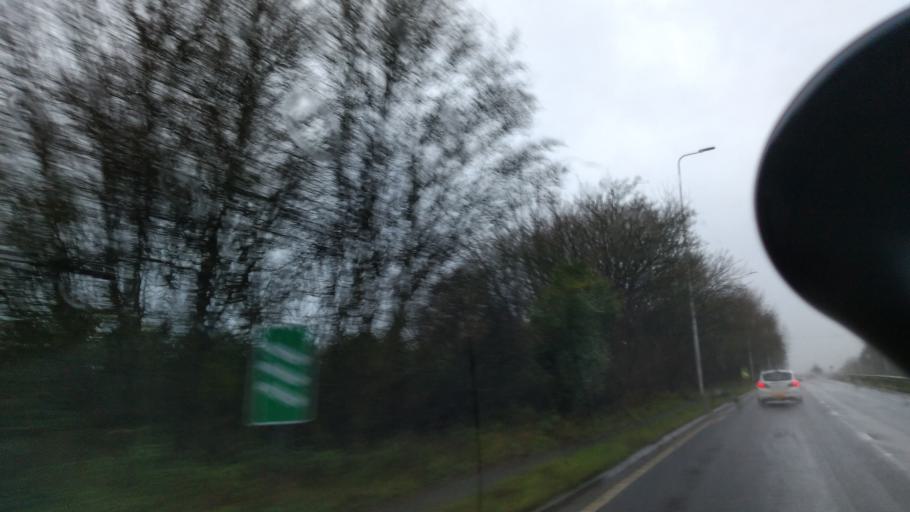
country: GB
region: England
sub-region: Brighton and Hove
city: Rottingdean
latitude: 50.8640
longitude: -0.0722
